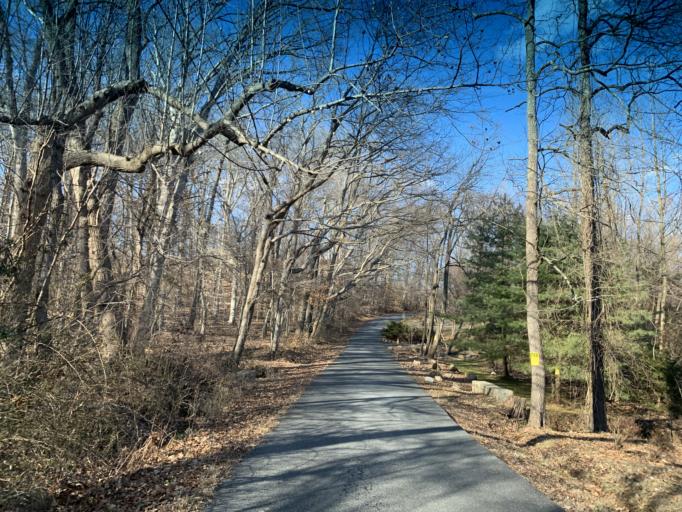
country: US
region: Maryland
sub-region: Baltimore County
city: Kingsville
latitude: 39.4288
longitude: -76.3839
